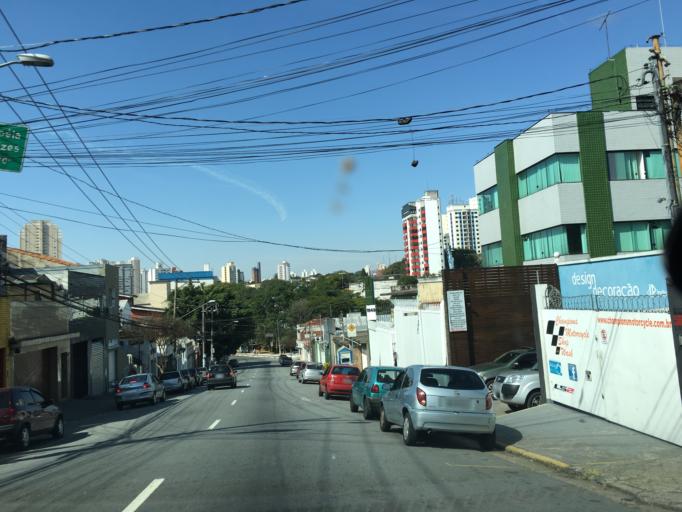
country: BR
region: Sao Paulo
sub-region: Sao Paulo
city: Sao Paulo
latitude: -23.5273
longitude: -46.7071
